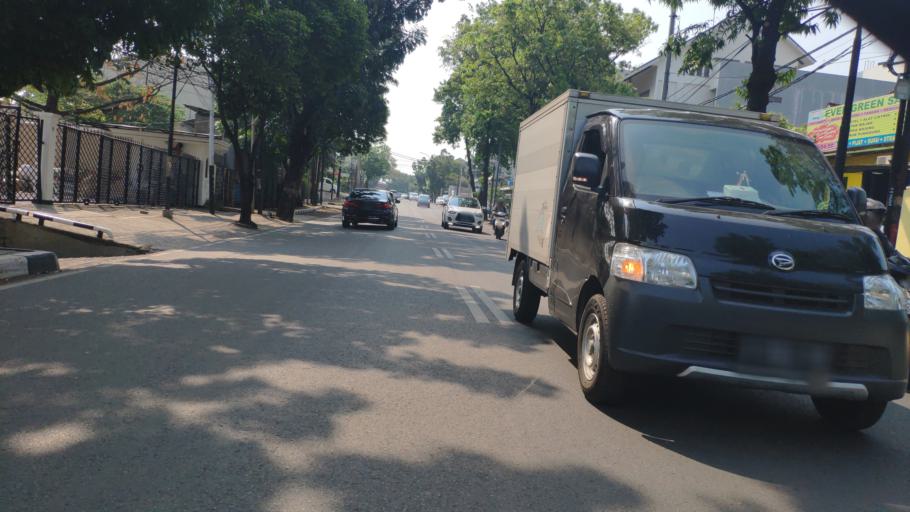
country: ID
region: Jakarta Raya
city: Jakarta
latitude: -6.2499
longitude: 106.7937
